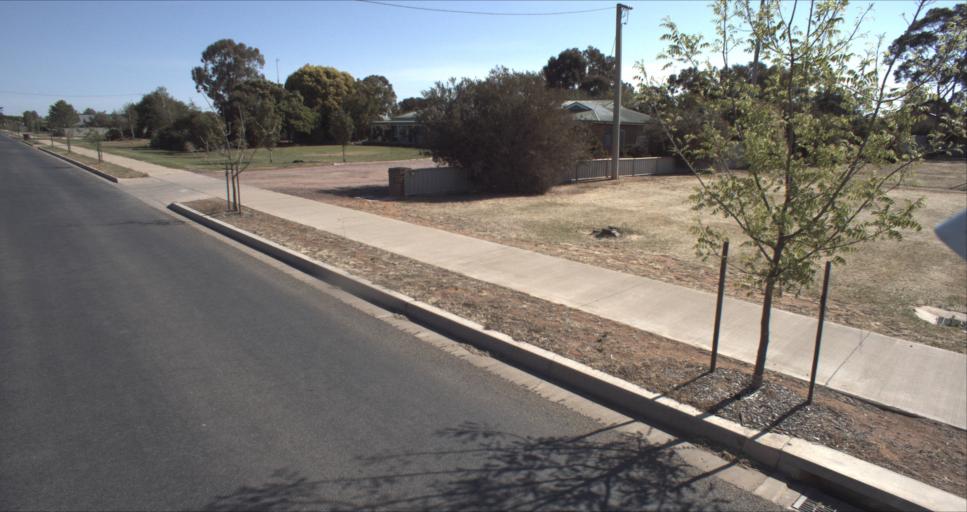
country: AU
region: New South Wales
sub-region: Leeton
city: Leeton
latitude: -34.5507
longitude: 146.4172
